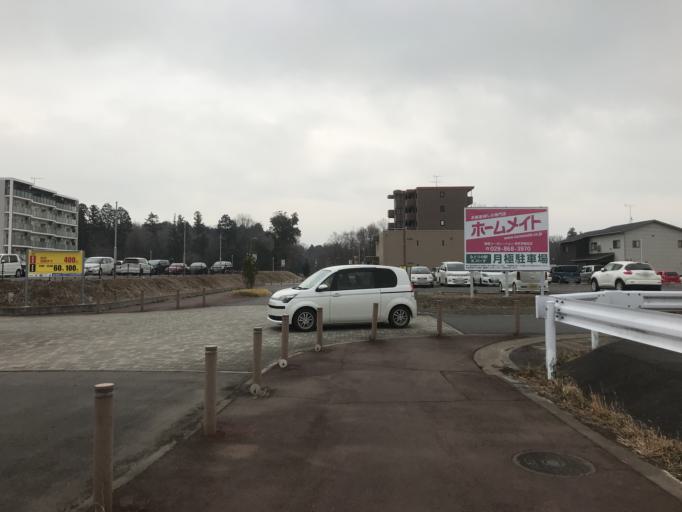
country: JP
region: Ibaraki
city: Mitsukaido
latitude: 36.0295
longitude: 140.0568
